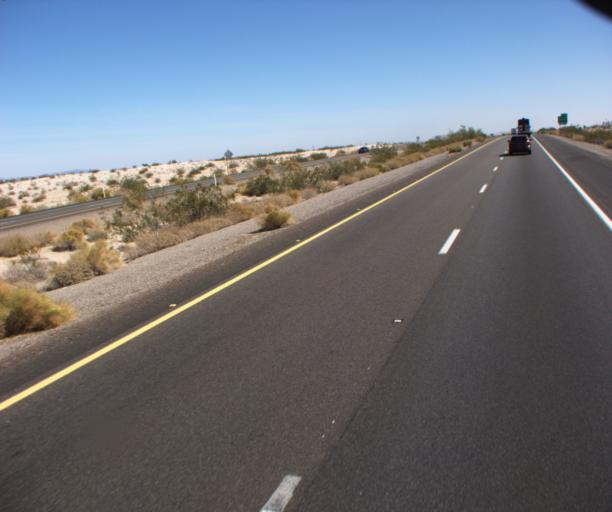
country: US
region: Arizona
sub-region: Yuma County
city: Wellton
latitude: 32.6583
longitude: -114.1566
